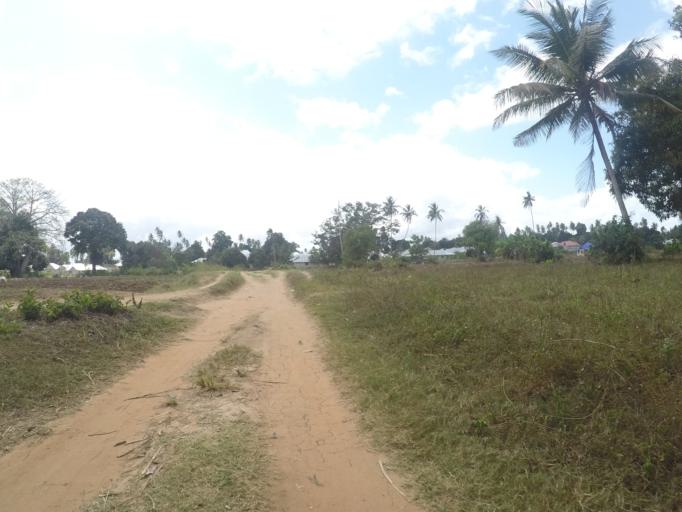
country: TZ
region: Zanzibar Urban/West
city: Zanzibar
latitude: -6.2055
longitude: 39.2394
